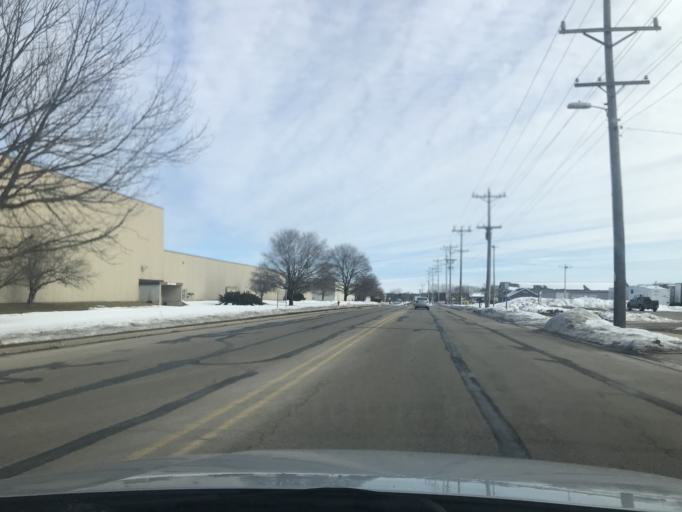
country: US
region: Wisconsin
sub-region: Oconto County
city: Oconto Falls
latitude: 44.8827
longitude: -88.1482
